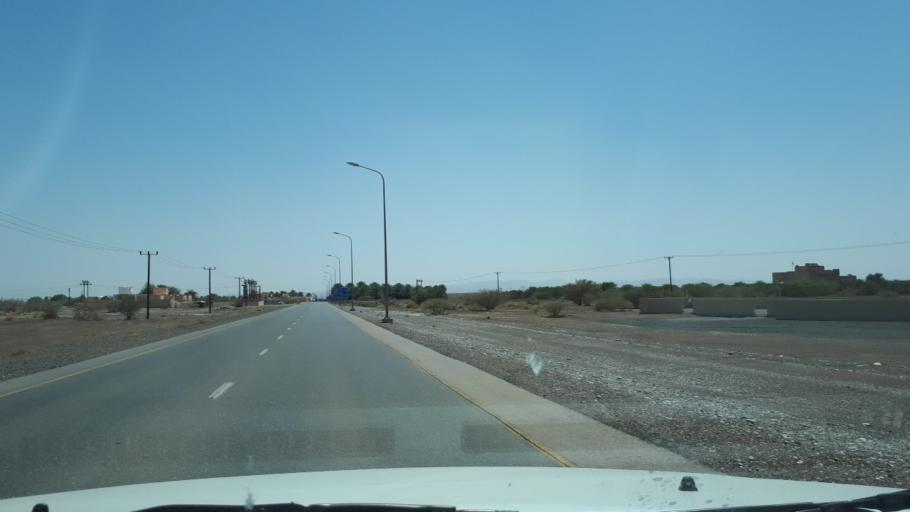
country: OM
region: Muhafazat ad Dakhiliyah
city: Bahla'
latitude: 22.9181
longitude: 57.2540
